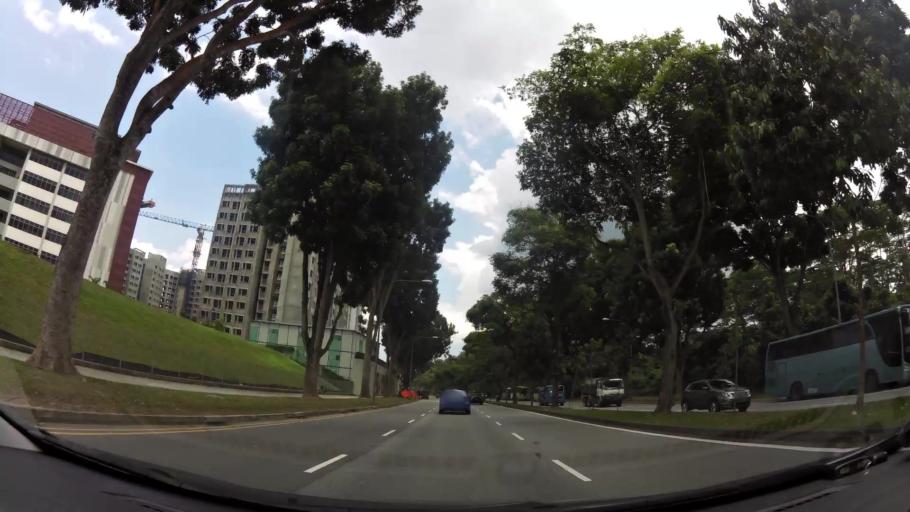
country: MY
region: Johor
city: Kampung Pasir Gudang Baru
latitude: 1.4234
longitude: 103.8516
